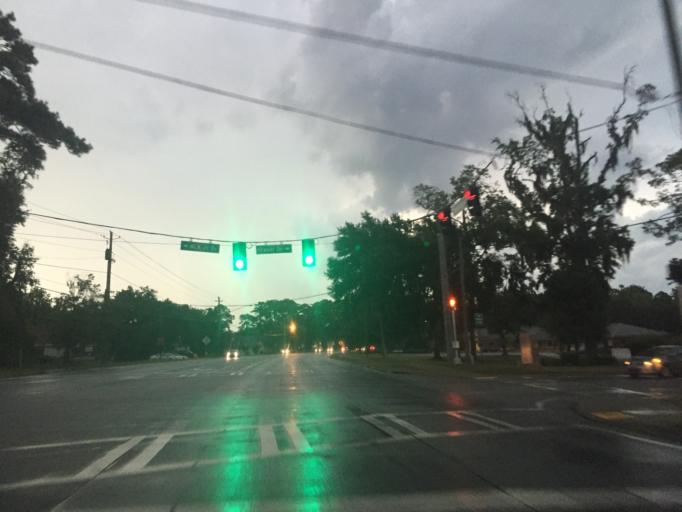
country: US
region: Georgia
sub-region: Liberty County
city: Hinesville
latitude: 31.8460
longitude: -81.5925
